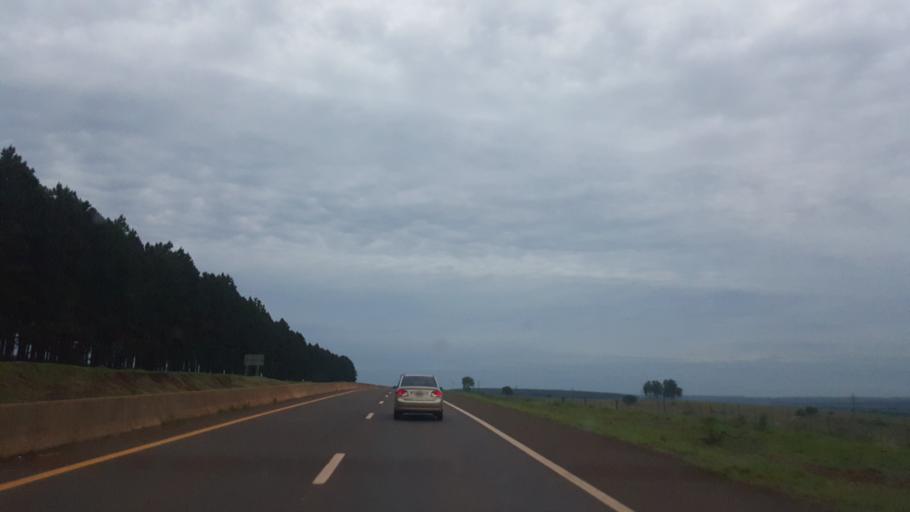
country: AR
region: Misiones
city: Garupa
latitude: -27.5741
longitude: -55.8469
